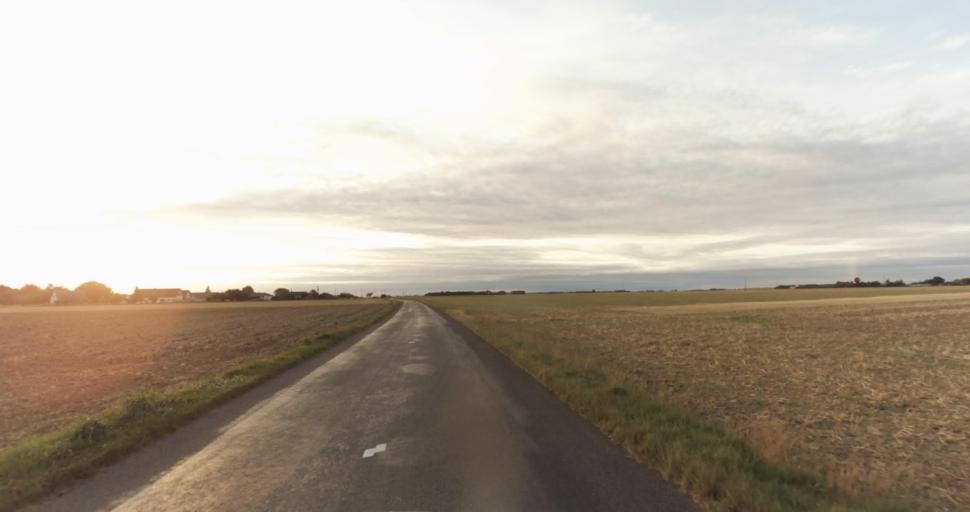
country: FR
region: Haute-Normandie
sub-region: Departement de l'Eure
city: La Madeleine-de-Nonancourt
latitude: 48.8702
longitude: 1.2214
